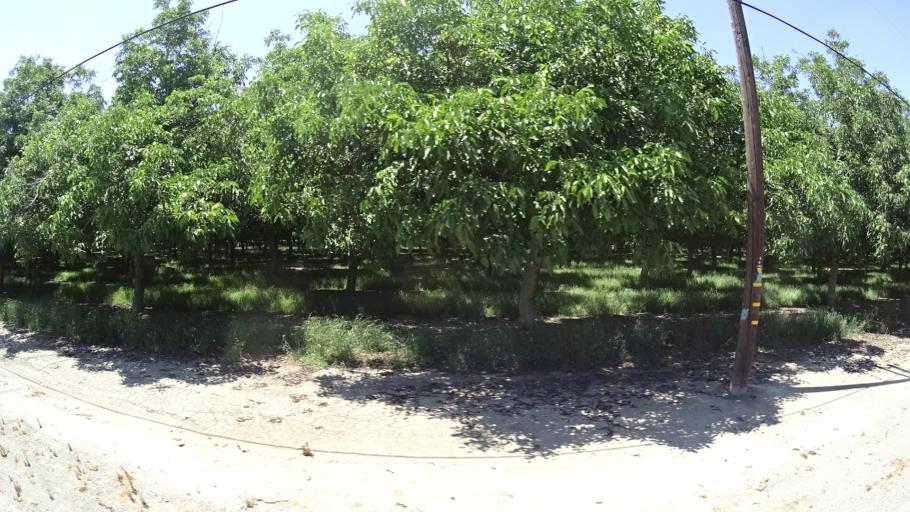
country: US
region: California
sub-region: Kings County
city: Lucerne
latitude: 36.4031
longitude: -119.6189
